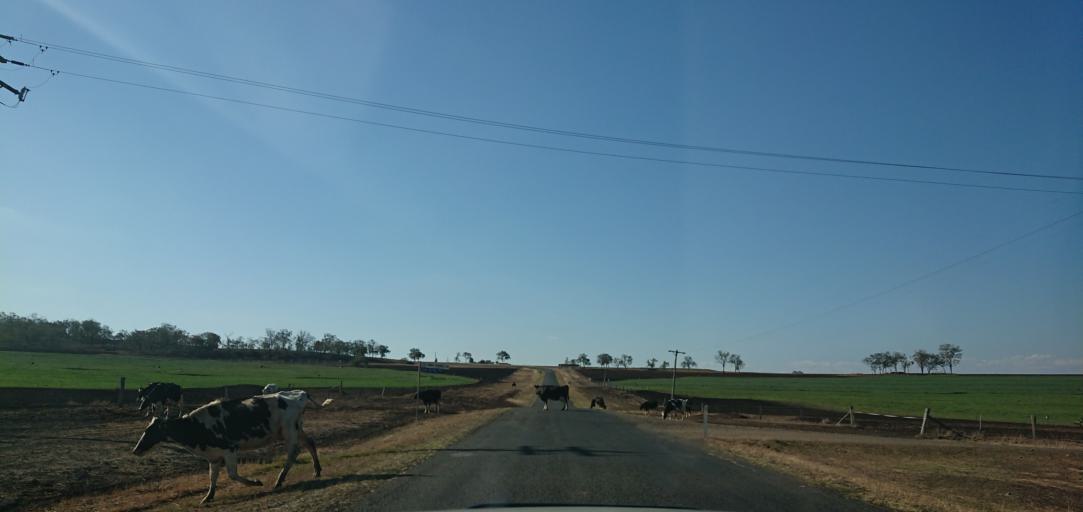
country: AU
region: Queensland
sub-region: Toowoomba
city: Westbrook
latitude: -27.7062
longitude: 151.7164
